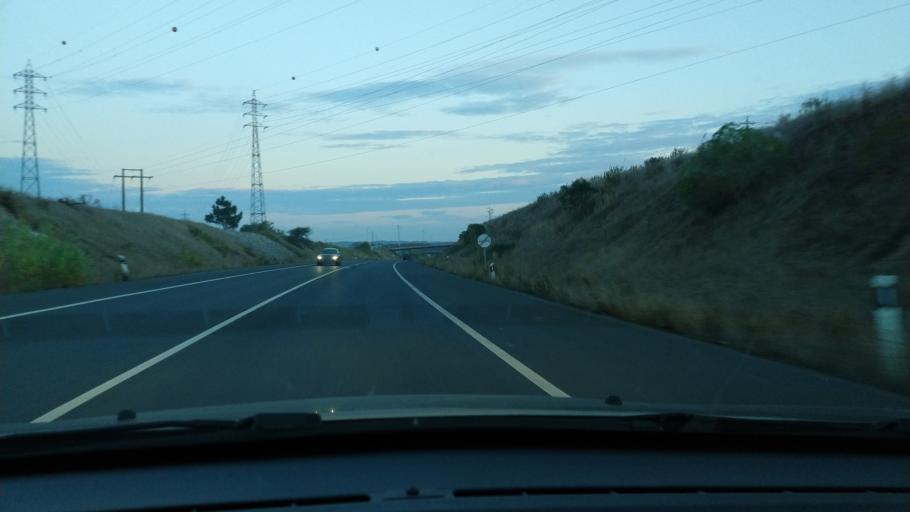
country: PT
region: Leiria
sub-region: Peniche
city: Atouguia da Baleia
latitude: 39.3278
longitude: -9.3182
